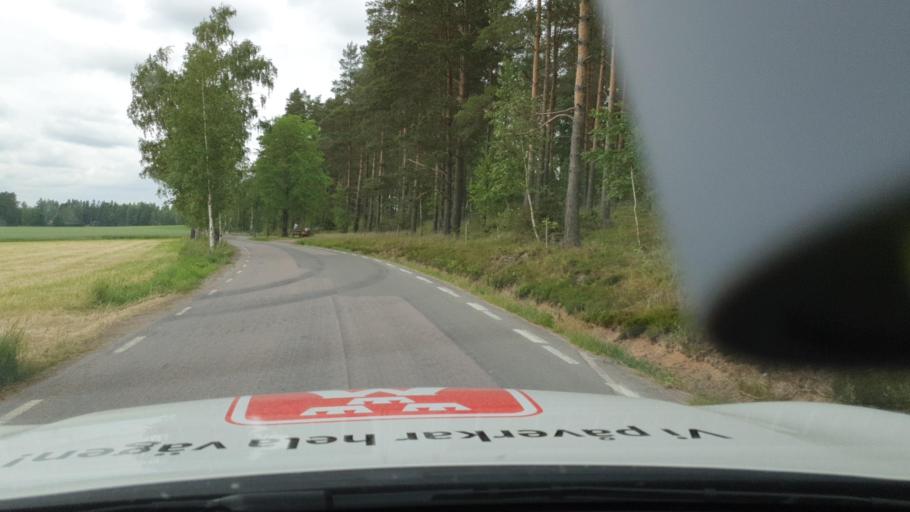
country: SE
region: Vaestra Goetaland
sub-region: Tidaholms Kommun
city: Olofstorp
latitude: 58.2425
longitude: 14.0959
